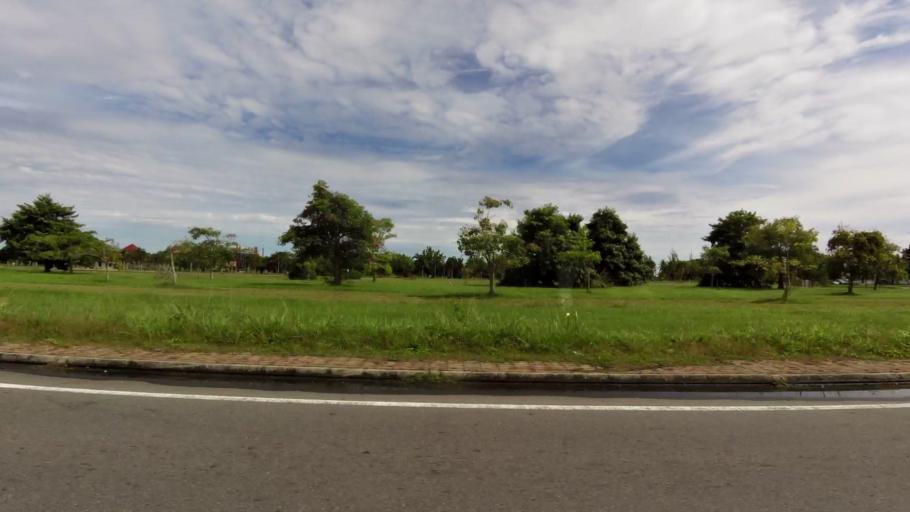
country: BN
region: Belait
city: Seria
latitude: 4.6154
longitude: 114.3289
